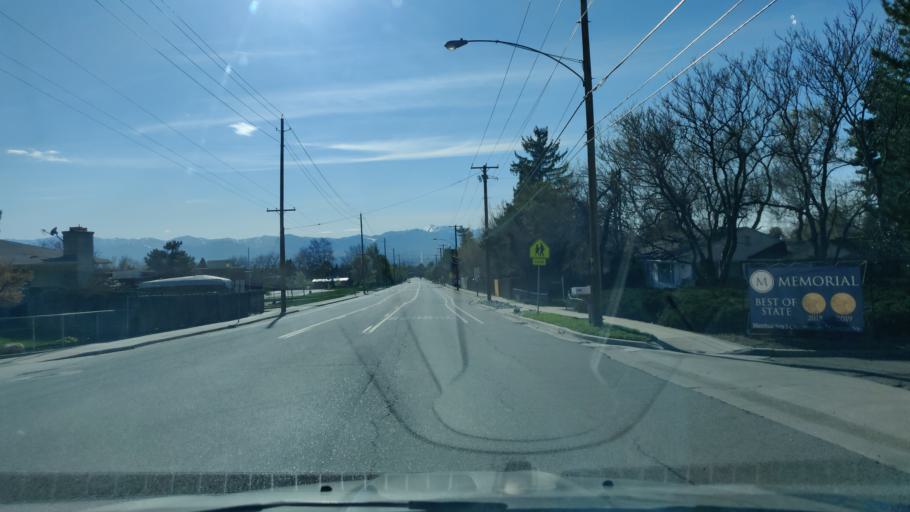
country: US
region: Utah
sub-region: Salt Lake County
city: Cottonwood Heights
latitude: 40.6094
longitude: -111.8048
